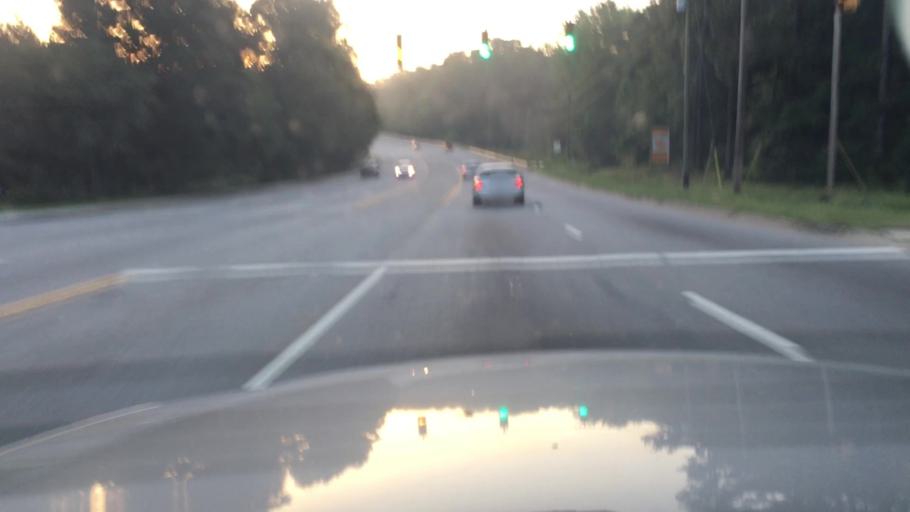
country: US
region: North Carolina
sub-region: Cumberland County
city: Fort Bragg
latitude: 35.0589
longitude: -78.9833
